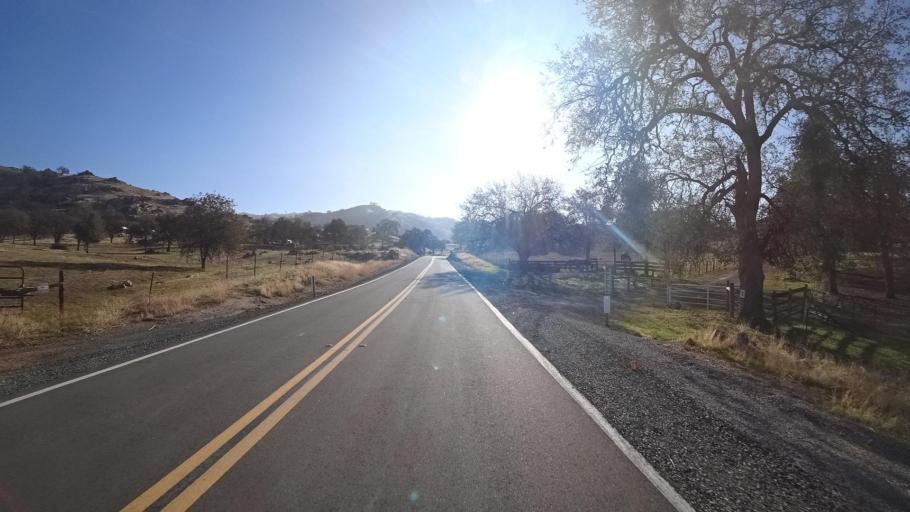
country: US
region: California
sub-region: Tulare County
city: Richgrove
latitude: 35.7081
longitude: -118.8379
